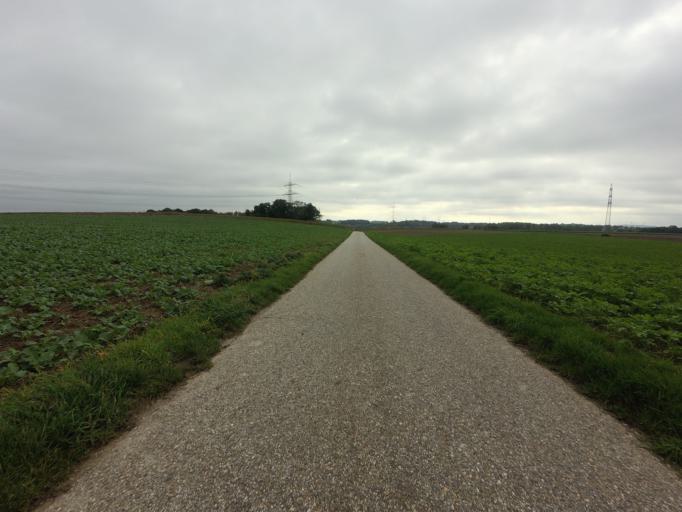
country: DE
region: North Rhine-Westphalia
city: Geilenkirchen
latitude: 50.9801
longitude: 6.1293
